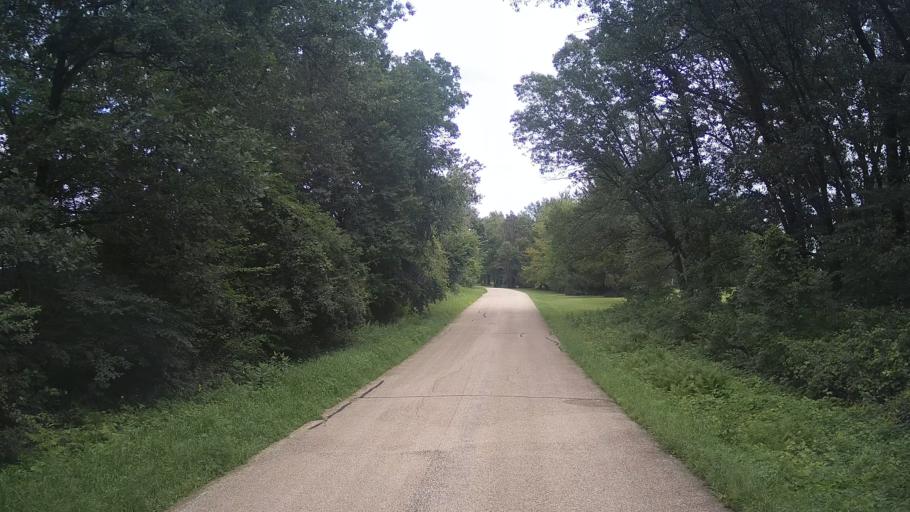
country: US
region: Wisconsin
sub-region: Adams County
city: Friendship
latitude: 44.0307
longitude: -89.9030
